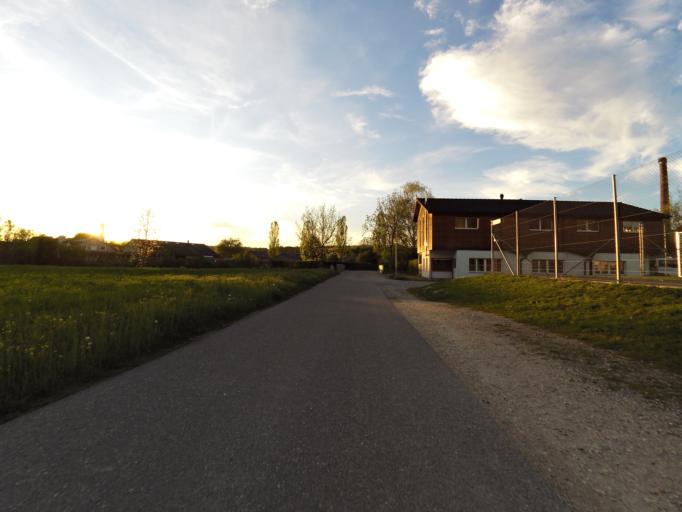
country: CH
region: Thurgau
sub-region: Frauenfeld District
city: Pfyn
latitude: 47.5930
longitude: 8.9664
